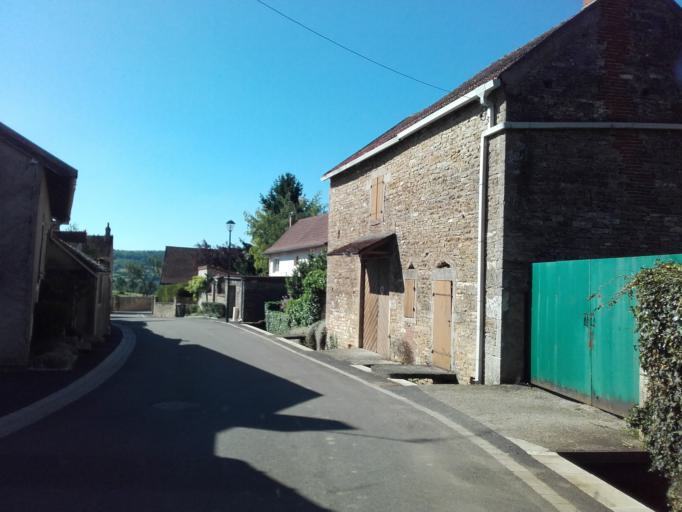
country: FR
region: Bourgogne
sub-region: Departement de la Cote-d'Or
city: Nolay
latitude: 46.9137
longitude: 4.6811
